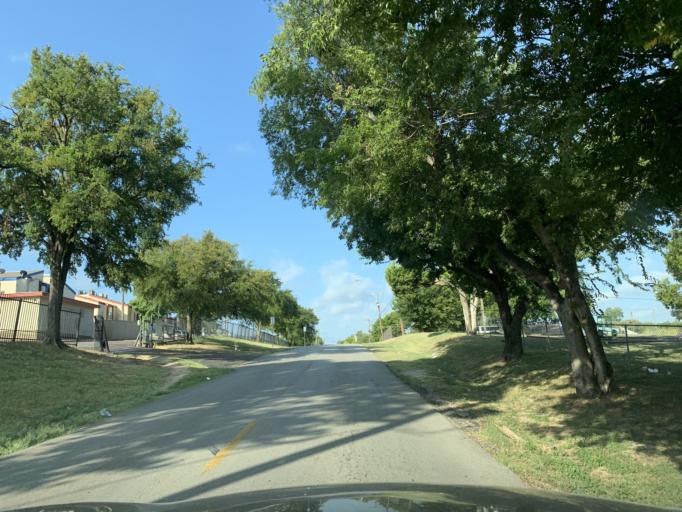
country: US
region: Texas
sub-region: Dallas County
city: Hutchins
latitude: 32.6785
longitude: -96.7653
